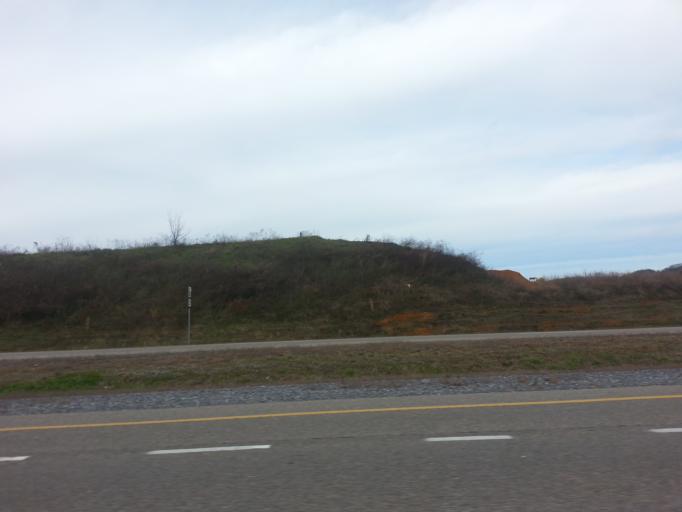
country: US
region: Tennessee
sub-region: Cocke County
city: Newport
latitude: 36.0039
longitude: -83.0920
